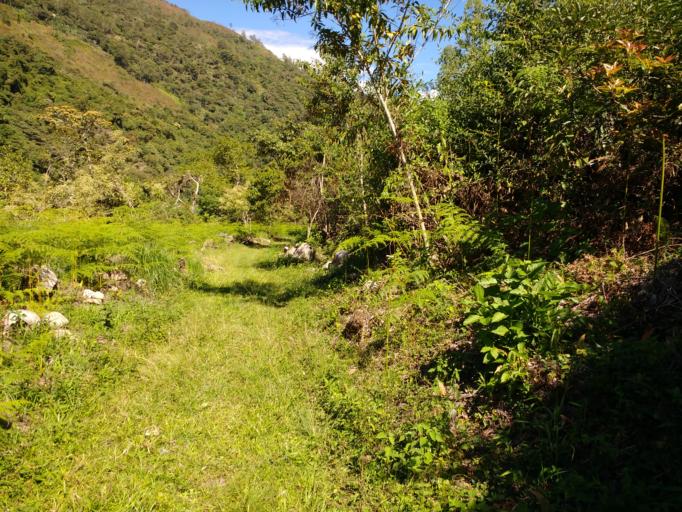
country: PE
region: Cusco
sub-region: Provincia de La Convencion
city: Maranura
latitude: -13.0039
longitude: -72.5295
